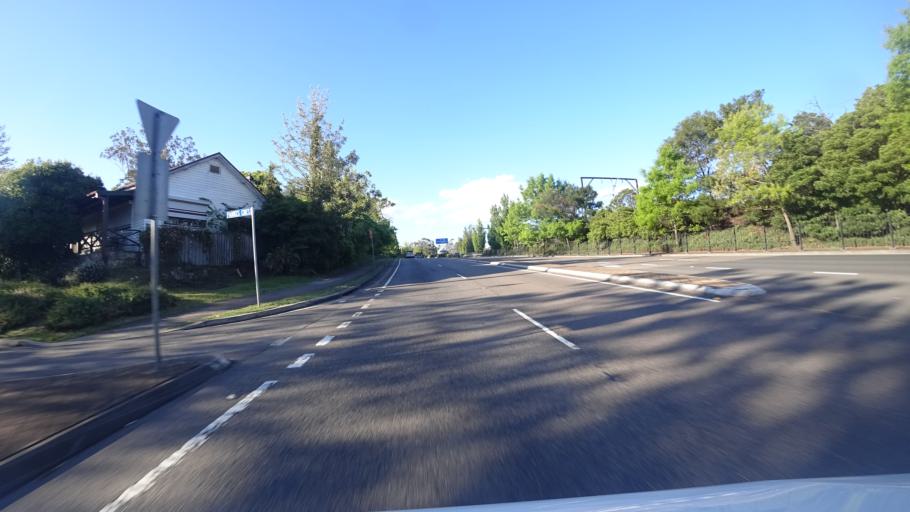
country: AU
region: New South Wales
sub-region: Blue Mountains Municipality
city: Hazelbrook
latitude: -33.6987
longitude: 150.5337
